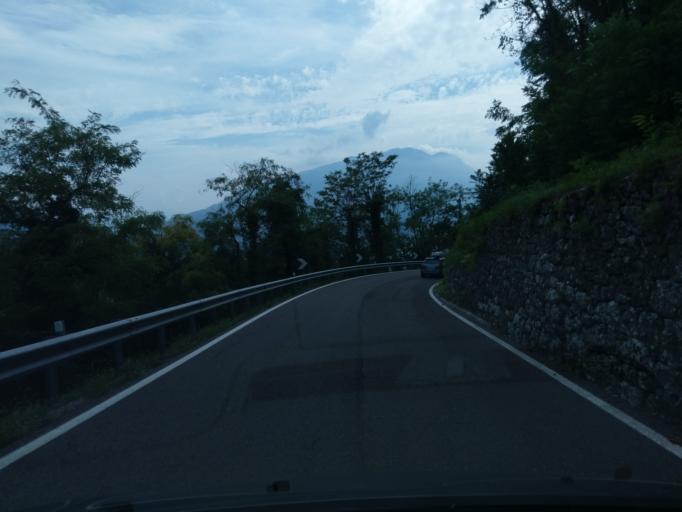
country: IT
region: Trentino-Alto Adige
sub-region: Provincia di Trento
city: Tenno
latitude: 45.9086
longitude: 10.8327
